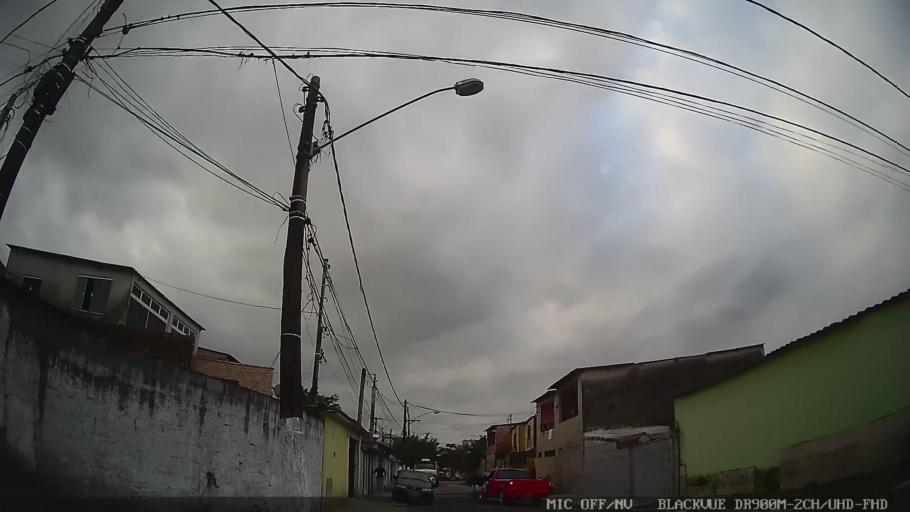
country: BR
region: Sao Paulo
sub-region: Santos
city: Santos
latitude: -23.9526
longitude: -46.2915
